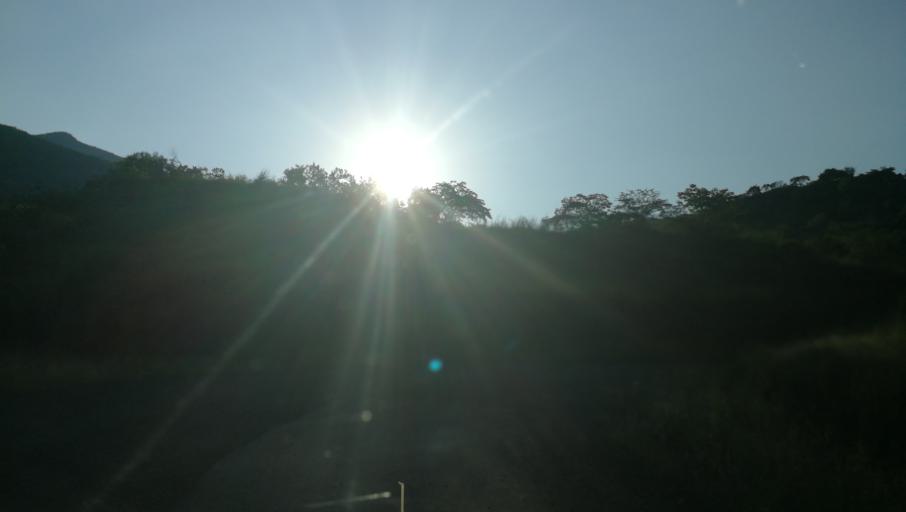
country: ET
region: Southern Nations, Nationalities, and People's Region
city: Areka
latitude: 6.8361
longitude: 37.2801
